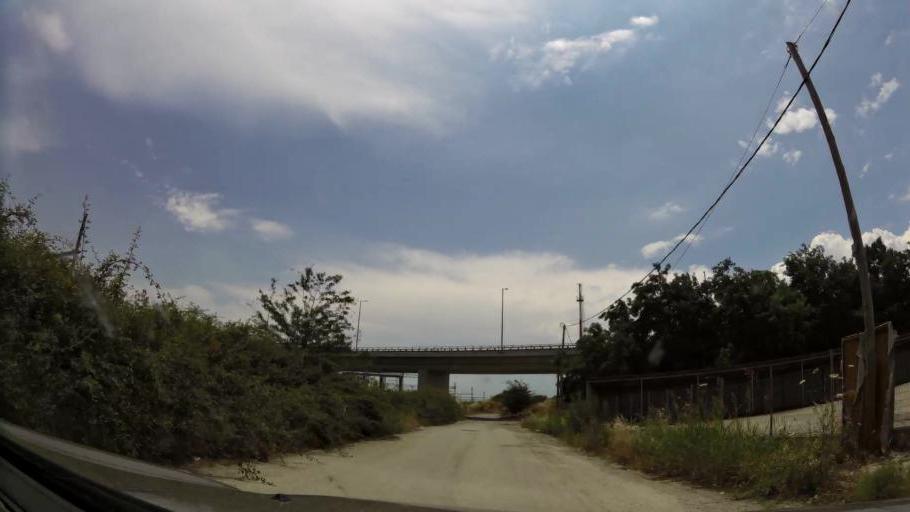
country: GR
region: Central Macedonia
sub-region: Nomos Pierias
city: Peristasi
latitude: 40.2635
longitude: 22.5304
